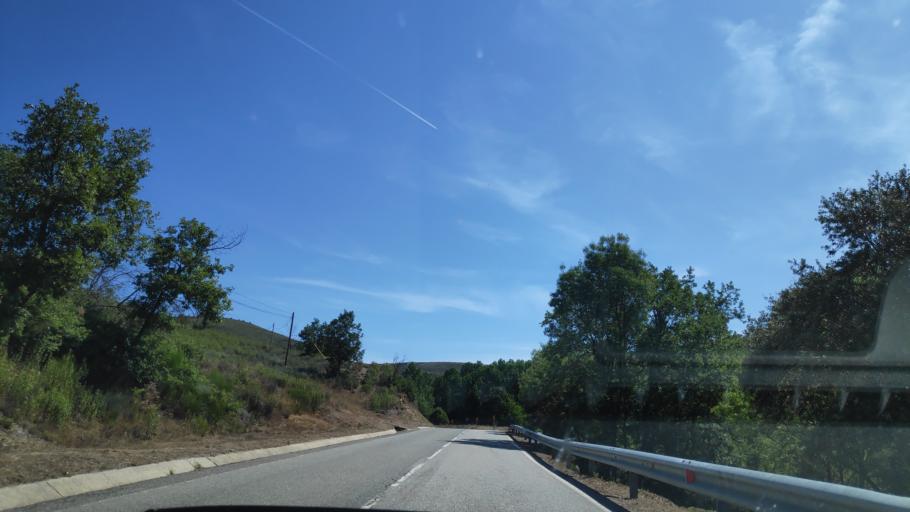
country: PT
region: Braganca
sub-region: Braganca Municipality
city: Braganca
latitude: 41.8881
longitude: -6.7322
